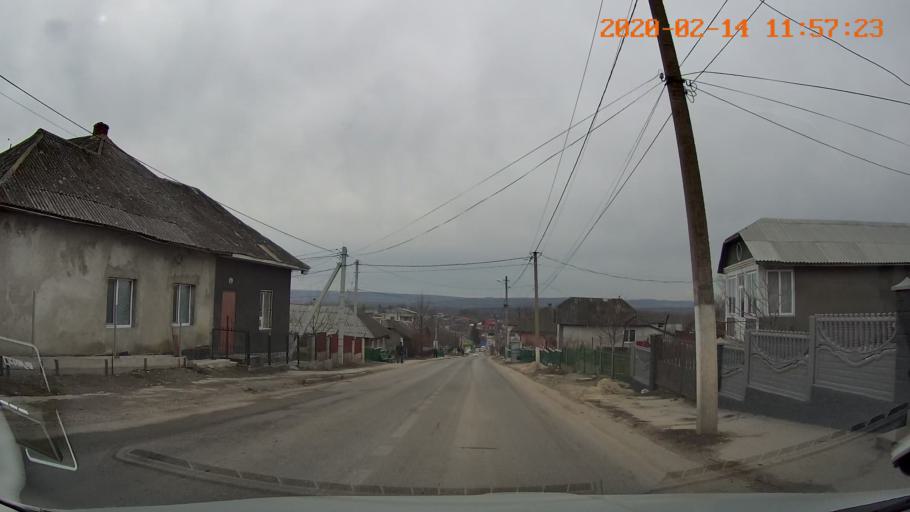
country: RO
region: Botosani
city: Radauti
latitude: 48.2661
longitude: 26.8100
